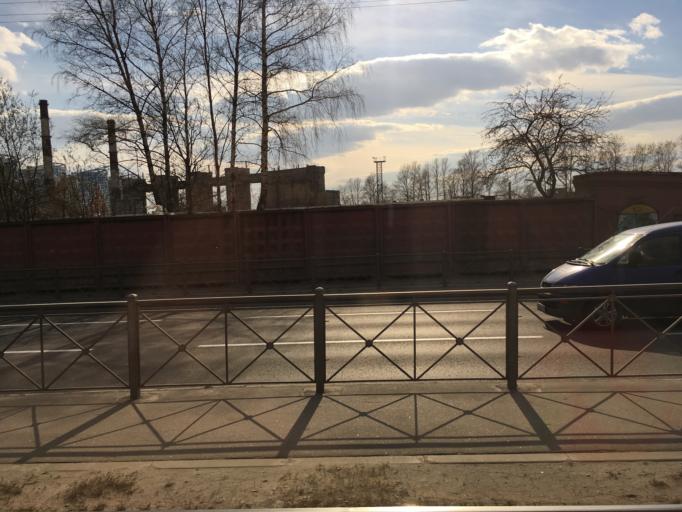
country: RU
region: St.-Petersburg
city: Obukhovo
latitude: 59.8974
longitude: 30.4607
